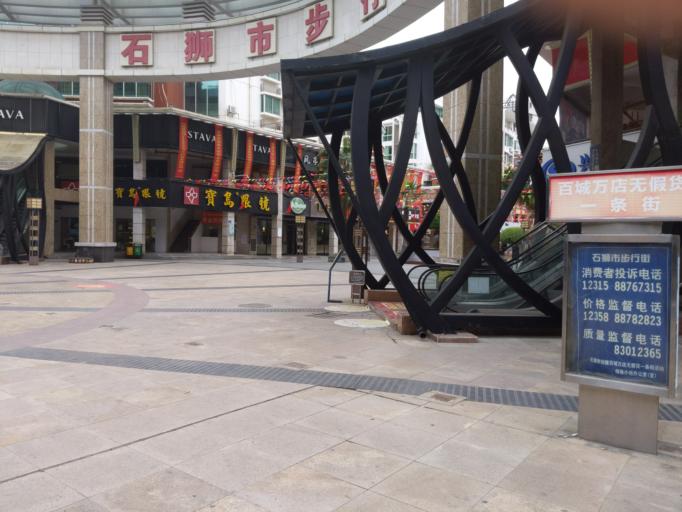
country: CN
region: Fujian
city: Shishi
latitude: 24.7352
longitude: 118.6283
